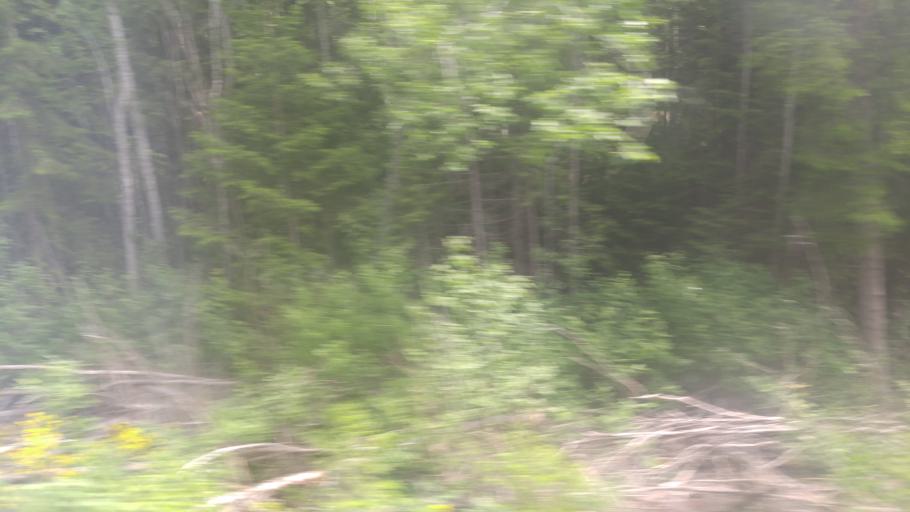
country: NO
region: Sor-Trondelag
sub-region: Selbu
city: Mebonden
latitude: 62.9536
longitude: 10.7373
